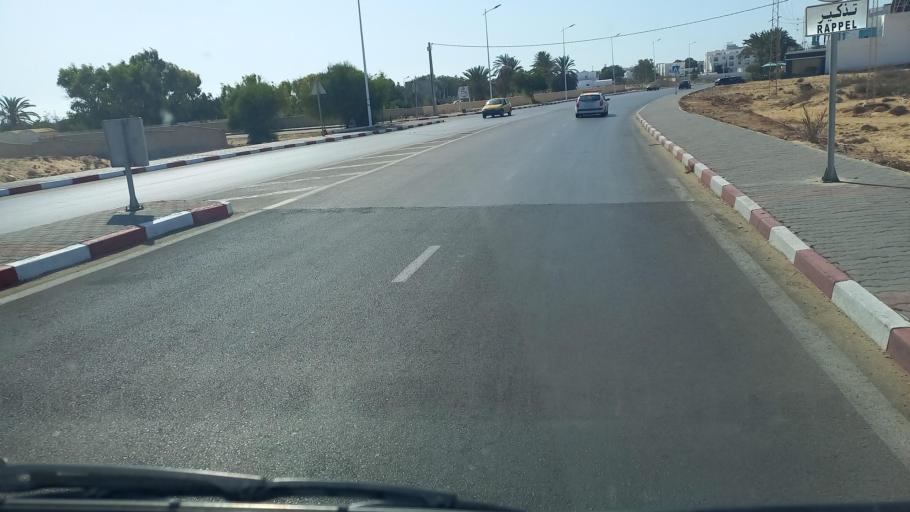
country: TN
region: Madanin
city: Midoun
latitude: 33.8474
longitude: 10.9869
